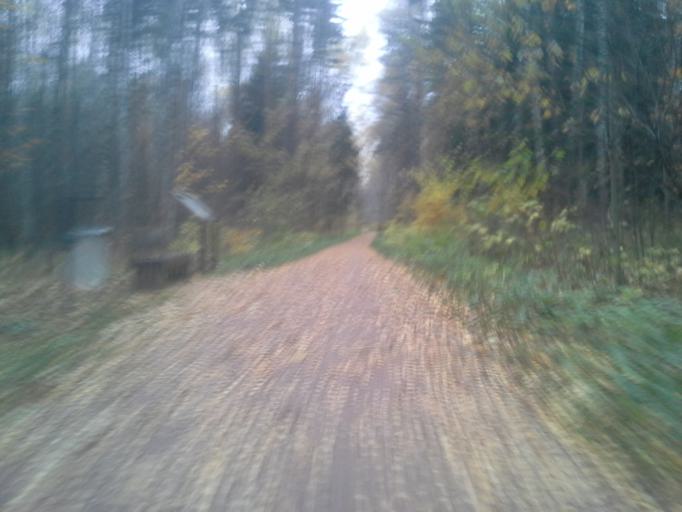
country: RU
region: Moskovskaya
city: Zarech'ye
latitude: 55.6654
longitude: 37.4010
